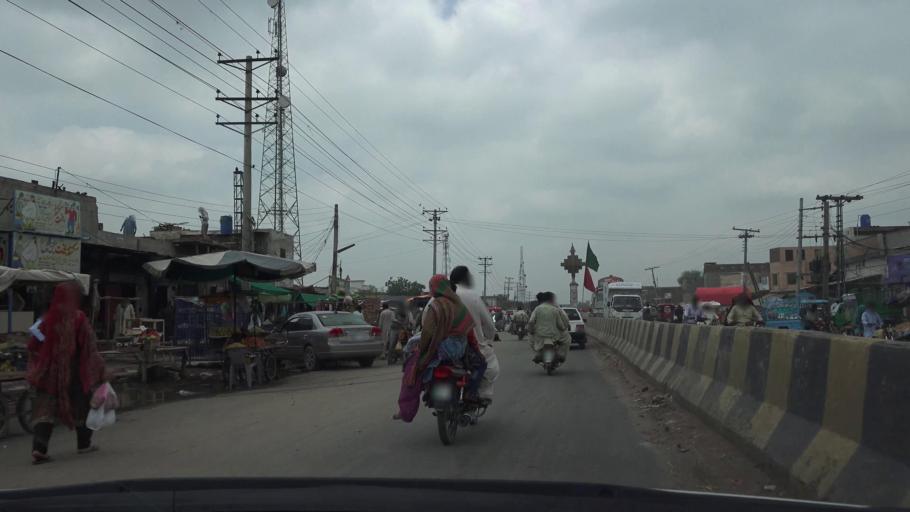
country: PK
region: Punjab
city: Faisalabad
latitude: 31.3877
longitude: 73.1998
